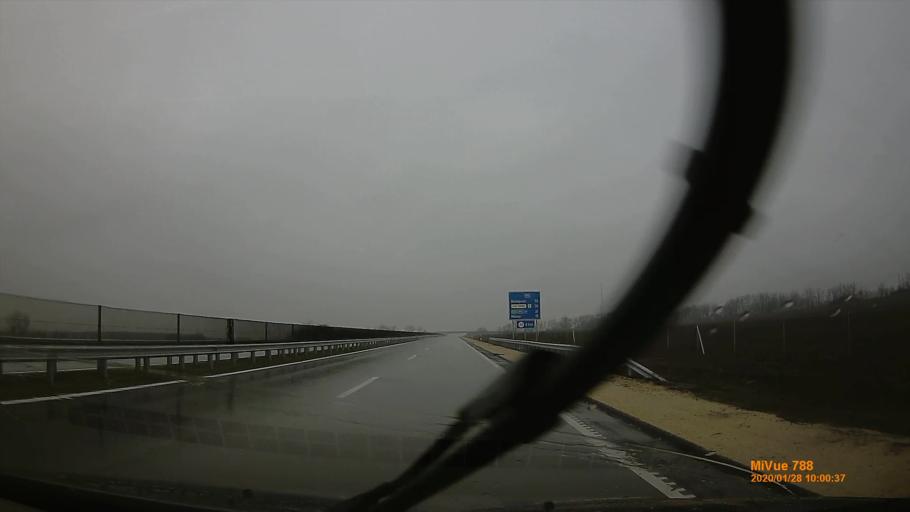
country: HU
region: Pest
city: Albertirsa
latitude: 47.2658
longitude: 19.6137
